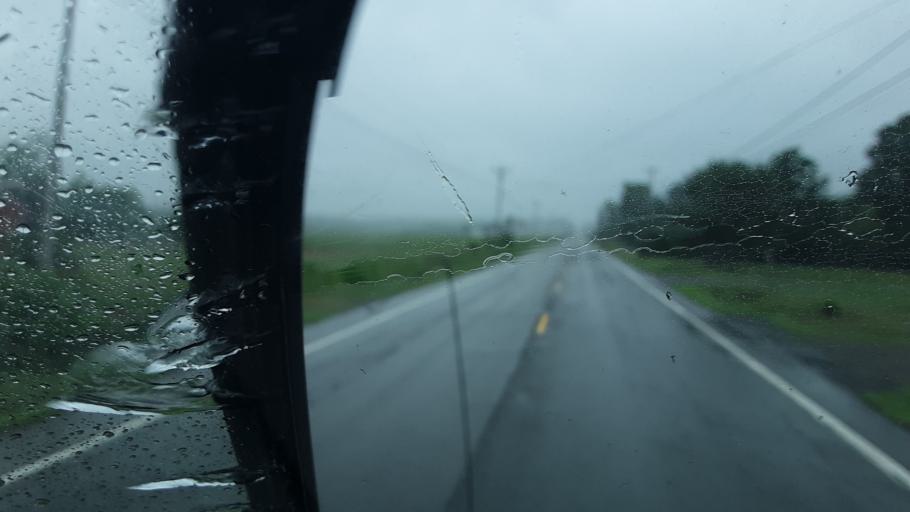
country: US
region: Maine
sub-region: Penobscot County
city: Patten
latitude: 46.0135
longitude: -68.4461
